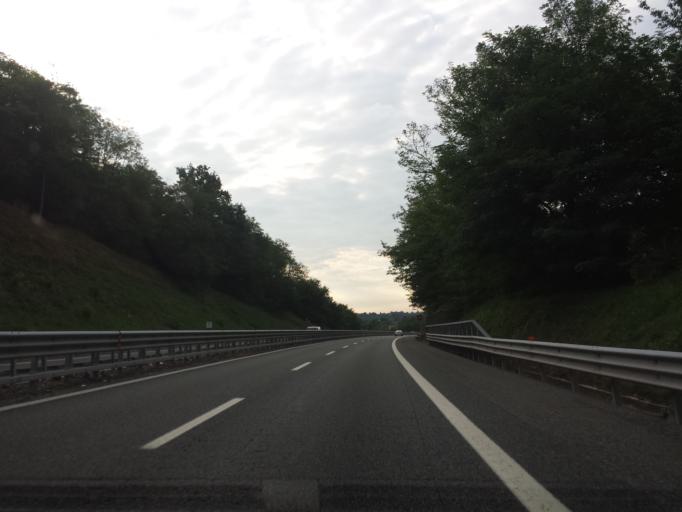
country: IT
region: Lombardy
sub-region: Provincia di Varese
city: Cavaria Con Premezzo
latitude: 45.6858
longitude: 8.7865
